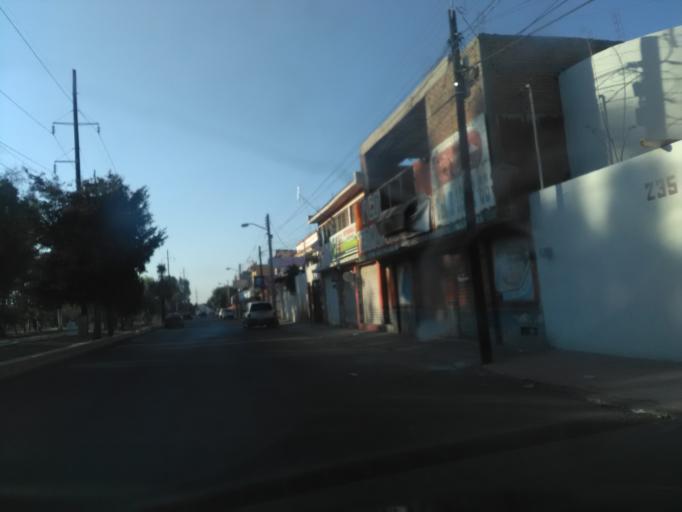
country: MX
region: Durango
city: Victoria de Durango
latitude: 24.0445
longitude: -104.6361
